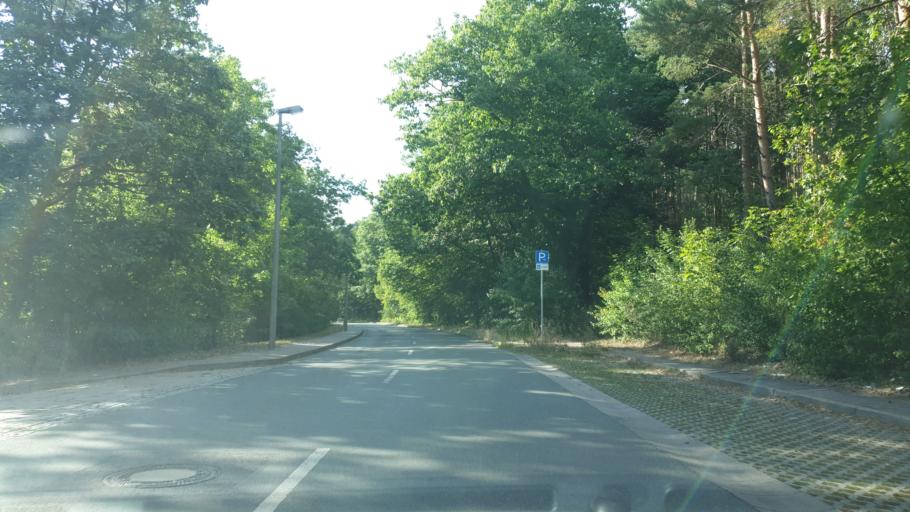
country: DE
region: Thuringia
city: Gera
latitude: 50.8708
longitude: 12.0514
